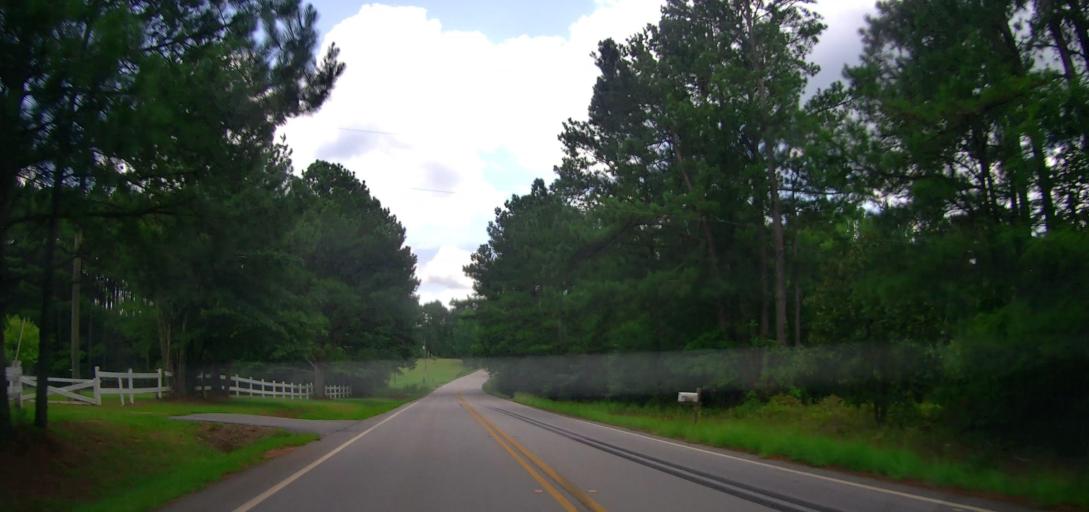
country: US
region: Georgia
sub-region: Meriwether County
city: Greenville
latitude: 33.0912
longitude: -84.7897
